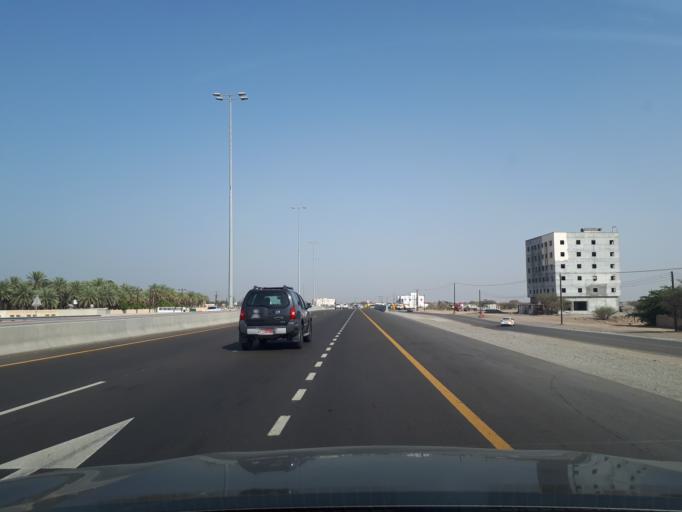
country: OM
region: Al Batinah
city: Al Sohar
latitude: 24.4165
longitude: 56.6282
